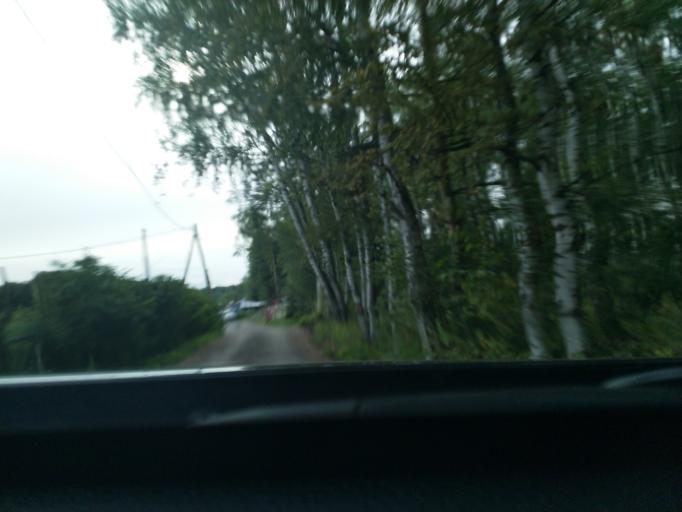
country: RU
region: Leningrad
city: Nikol'skoye
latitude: 59.7268
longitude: 30.7710
